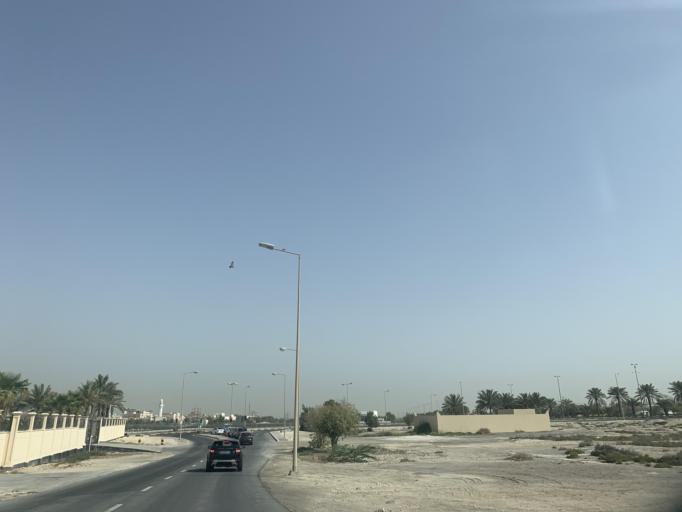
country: BH
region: Northern
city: Ar Rifa'
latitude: 26.1491
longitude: 50.5368
